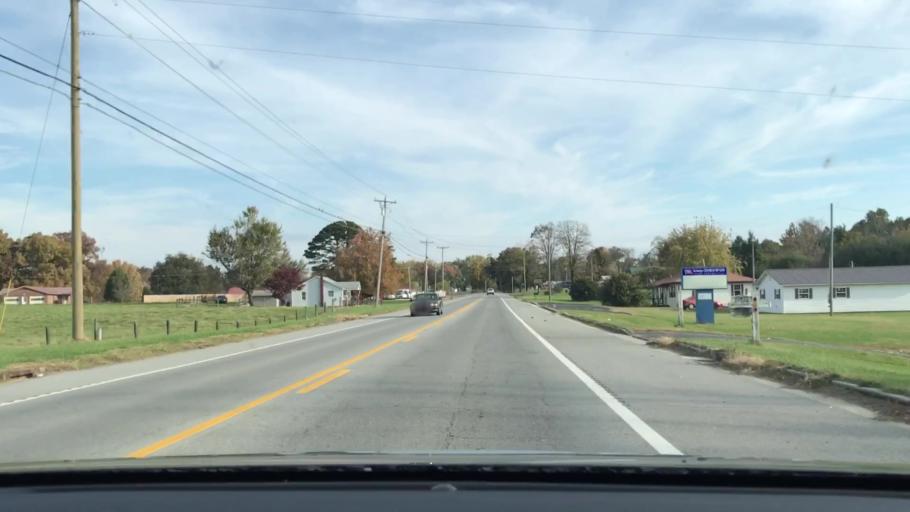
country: US
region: Tennessee
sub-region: Fentress County
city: Grimsley
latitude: 36.2562
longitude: -84.9891
